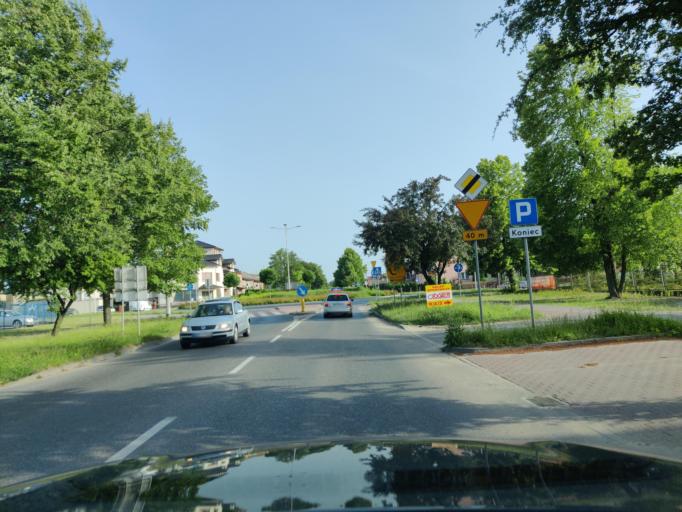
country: PL
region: Masovian Voivodeship
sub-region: Powiat wyszkowski
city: Wyszkow
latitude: 52.6071
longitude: 21.4545
